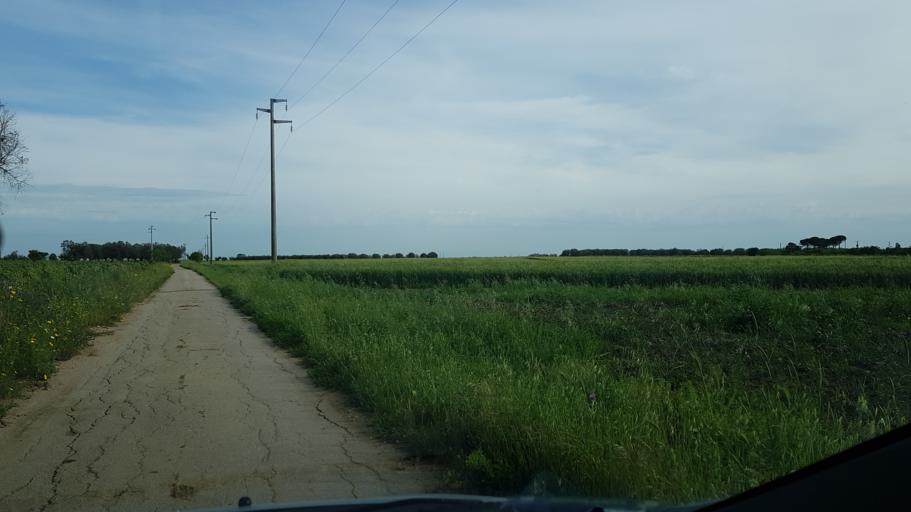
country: IT
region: Apulia
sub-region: Provincia di Brindisi
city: Tuturano
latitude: 40.5129
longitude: 17.9608
